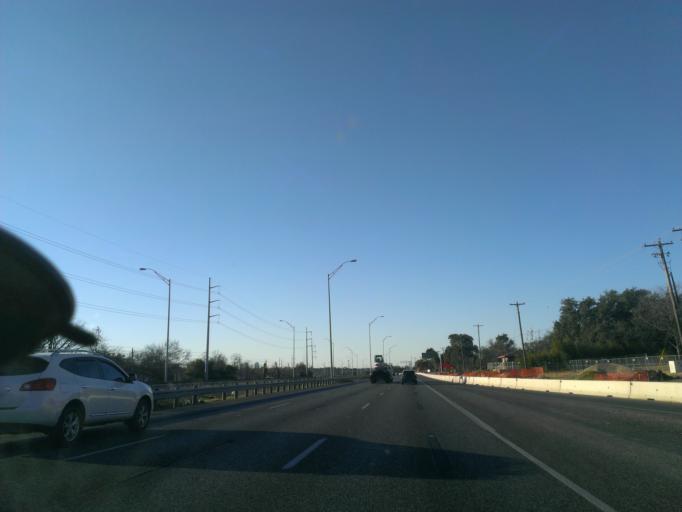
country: US
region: Texas
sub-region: Travis County
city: Austin
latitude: 30.3071
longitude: -97.7581
